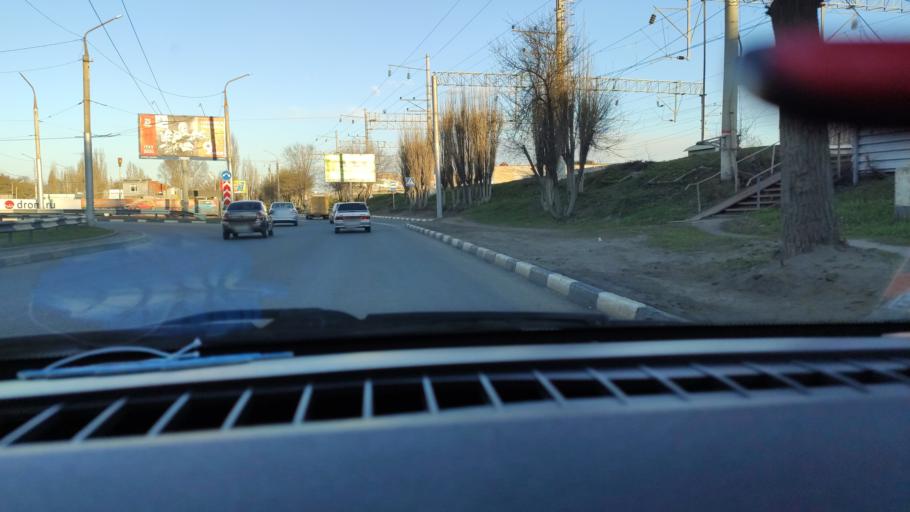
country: RU
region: Saratov
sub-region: Saratovskiy Rayon
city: Saratov
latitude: 51.5805
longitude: 45.9784
